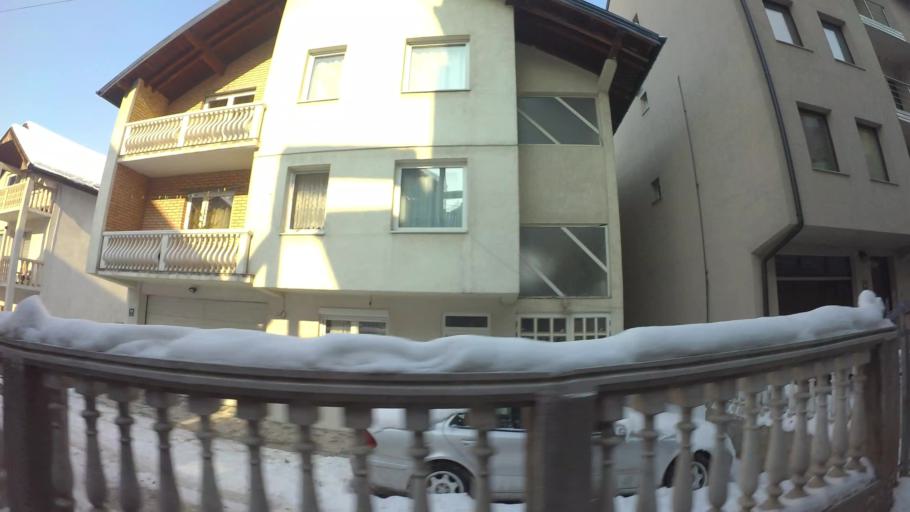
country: BA
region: Federation of Bosnia and Herzegovina
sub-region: Kanton Sarajevo
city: Sarajevo
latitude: 43.8447
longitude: 18.3867
